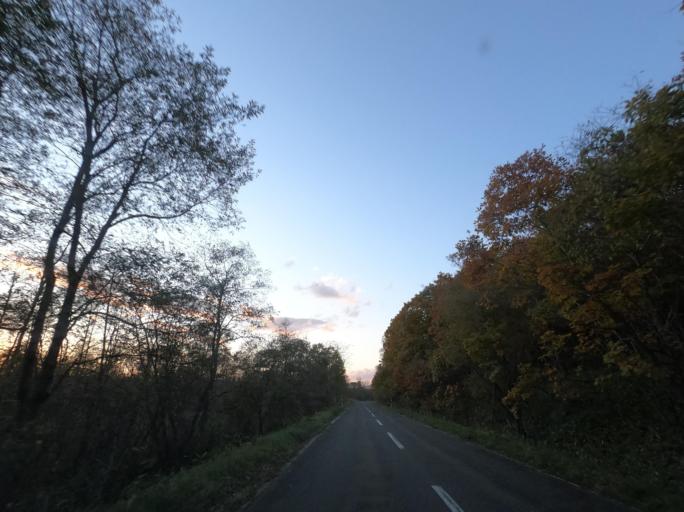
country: JP
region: Hokkaido
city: Kushiro
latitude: 43.2179
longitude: 144.4488
